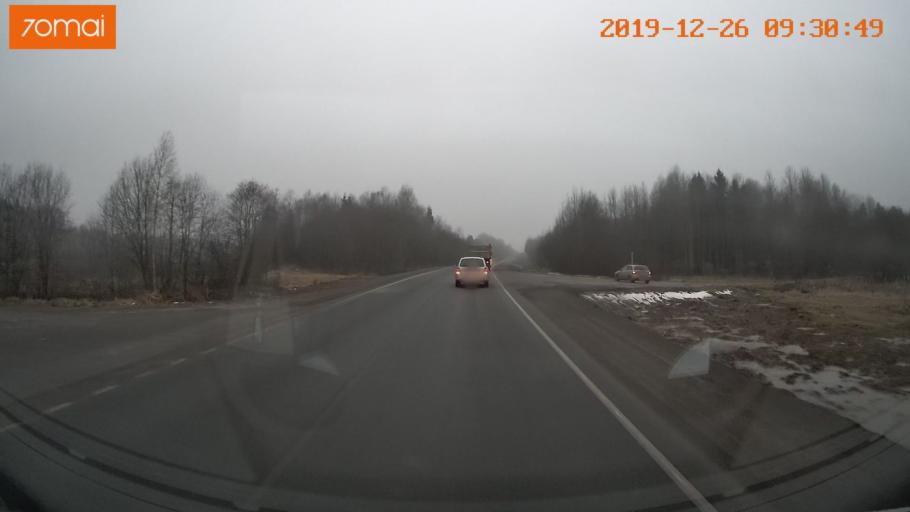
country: RU
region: Vologda
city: Gryazovets
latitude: 59.0637
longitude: 40.1352
